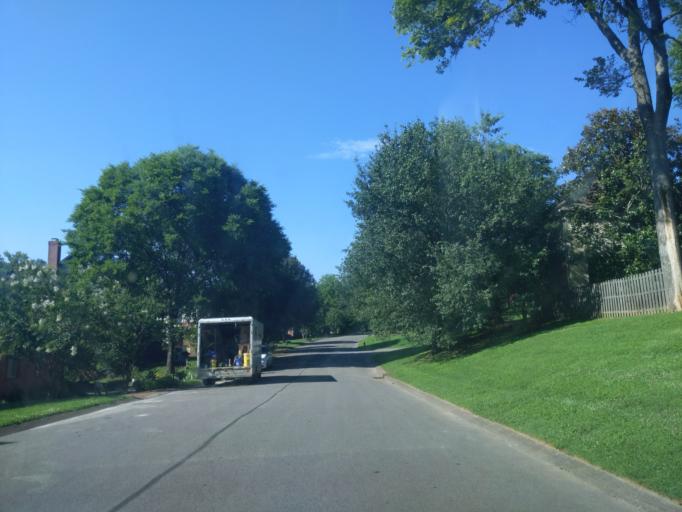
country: US
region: Tennessee
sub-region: Williamson County
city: Brentwood Estates
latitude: 36.0236
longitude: -86.7552
